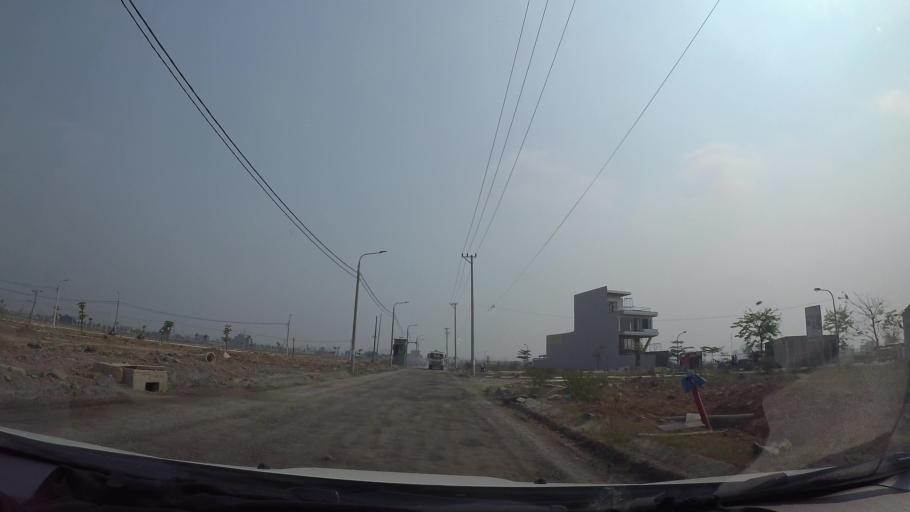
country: VN
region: Da Nang
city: Ngu Hanh Son
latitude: 16.0004
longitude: 108.2349
